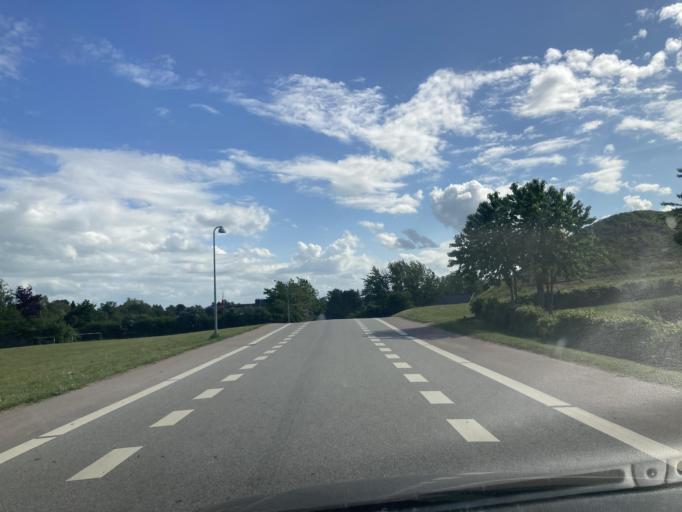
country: DK
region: Capital Region
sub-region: Gribskov Kommune
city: Helsinge
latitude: 56.0099
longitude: 12.1115
